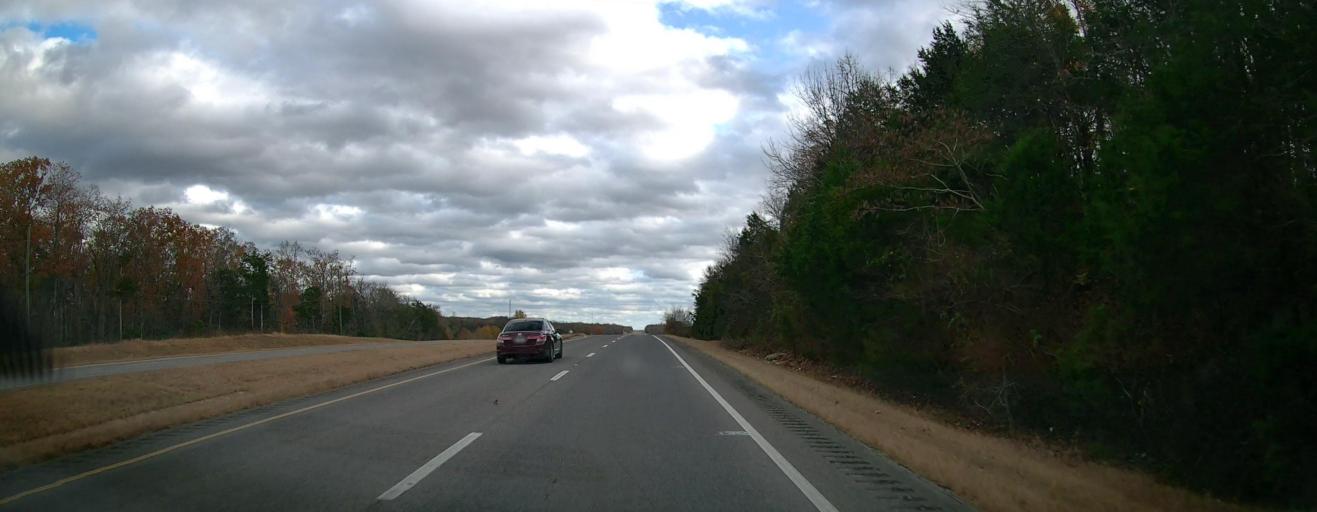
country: US
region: Alabama
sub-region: Morgan County
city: Danville
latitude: 34.4143
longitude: -87.1570
